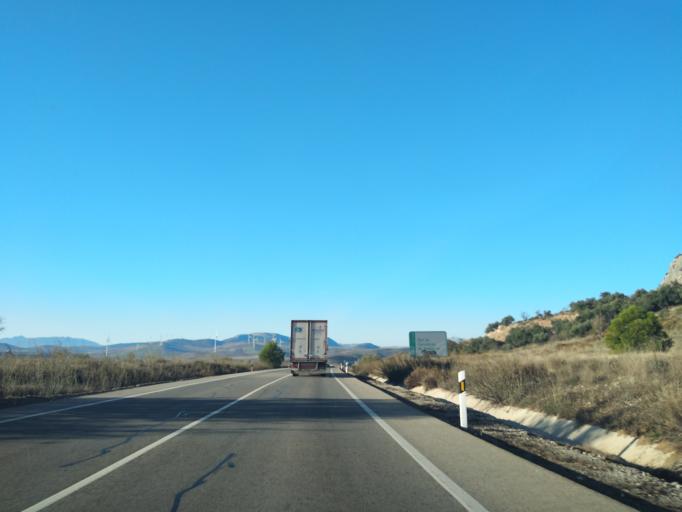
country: ES
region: Andalusia
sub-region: Provincia de Malaga
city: Teba
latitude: 36.9695
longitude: -4.8417
